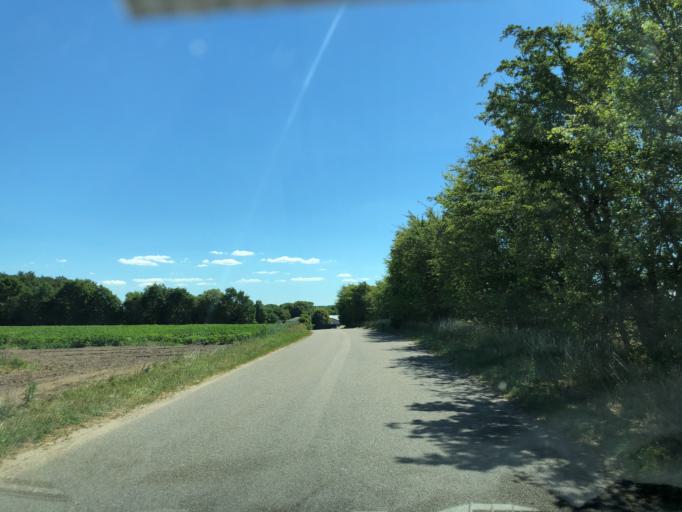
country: DK
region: Central Jutland
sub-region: Viborg Kommune
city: Viborg
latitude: 56.5571
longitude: 9.4216
